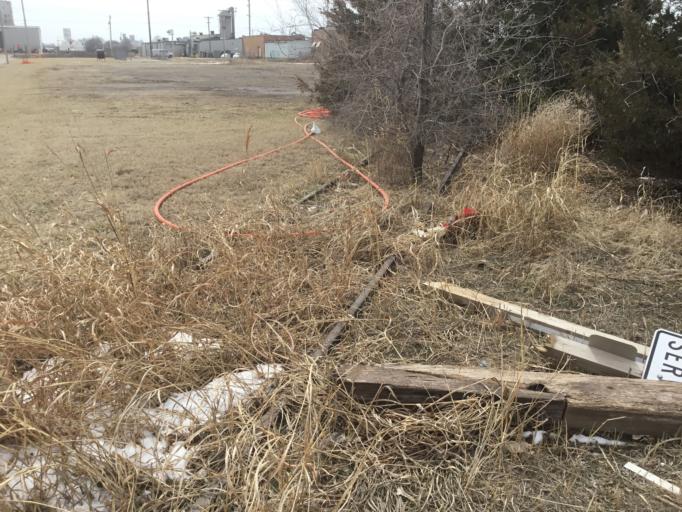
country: US
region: Kansas
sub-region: Sedgwick County
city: Wichita
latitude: 37.7390
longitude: -97.3311
